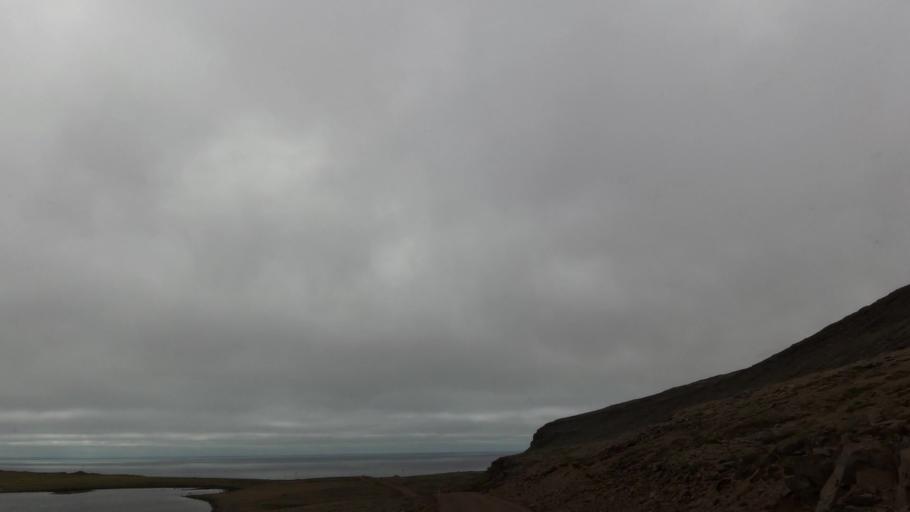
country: IS
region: West
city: Olafsvik
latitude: 65.5266
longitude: -24.4311
